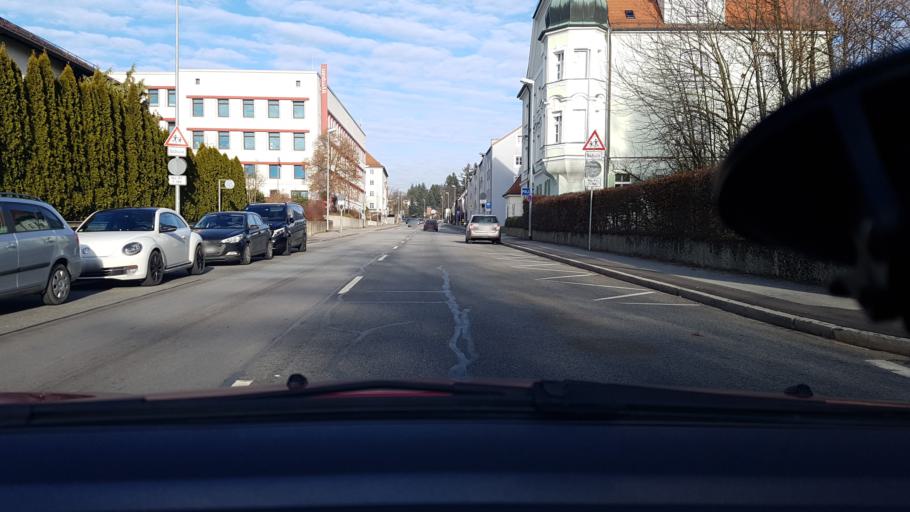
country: DE
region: Bavaria
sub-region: Lower Bavaria
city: Pfarrkirchen
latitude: 48.4348
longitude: 12.9371
